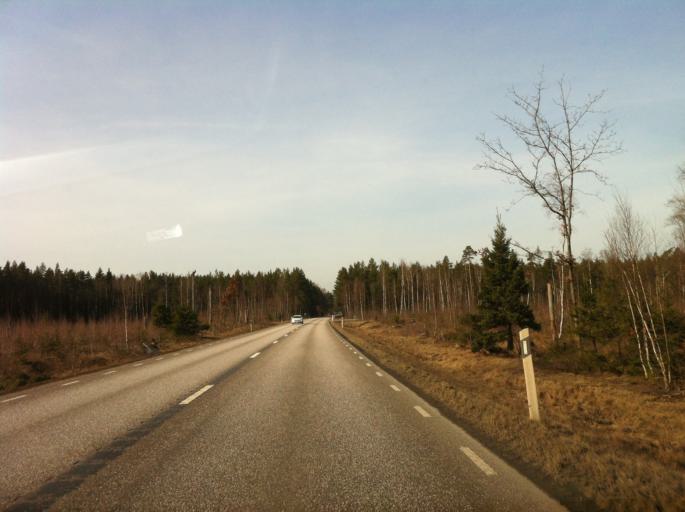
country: SE
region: Vaestra Goetaland
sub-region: Tidaholms Kommun
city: Tidaholm
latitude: 58.2124
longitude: 13.8656
